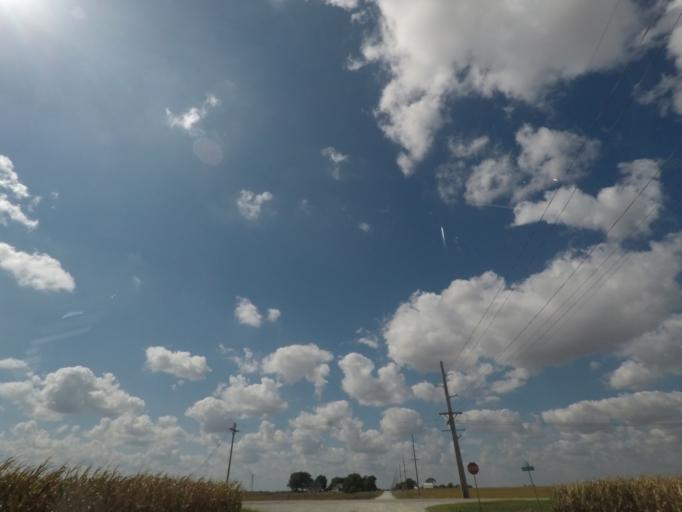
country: US
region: Iowa
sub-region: Story County
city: Nevada
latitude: 42.0344
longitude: -93.4053
